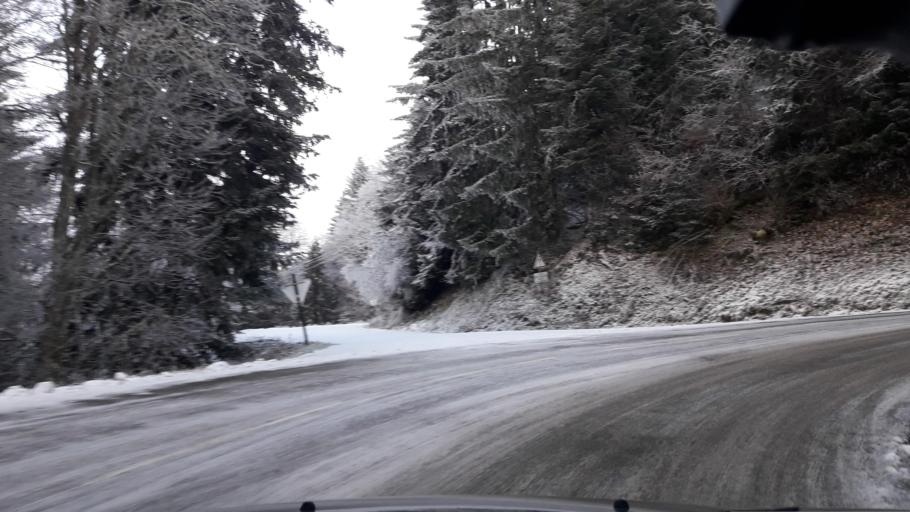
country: FR
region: Rhone-Alpes
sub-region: Departement de l'Isere
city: Allevard
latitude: 45.3997
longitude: 6.1045
